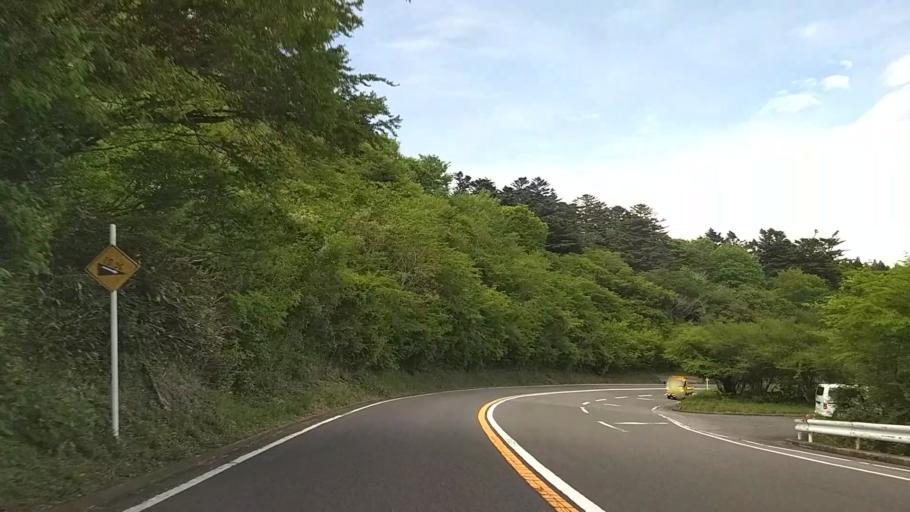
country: JP
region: Kanagawa
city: Yugawara
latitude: 35.2048
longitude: 139.0887
